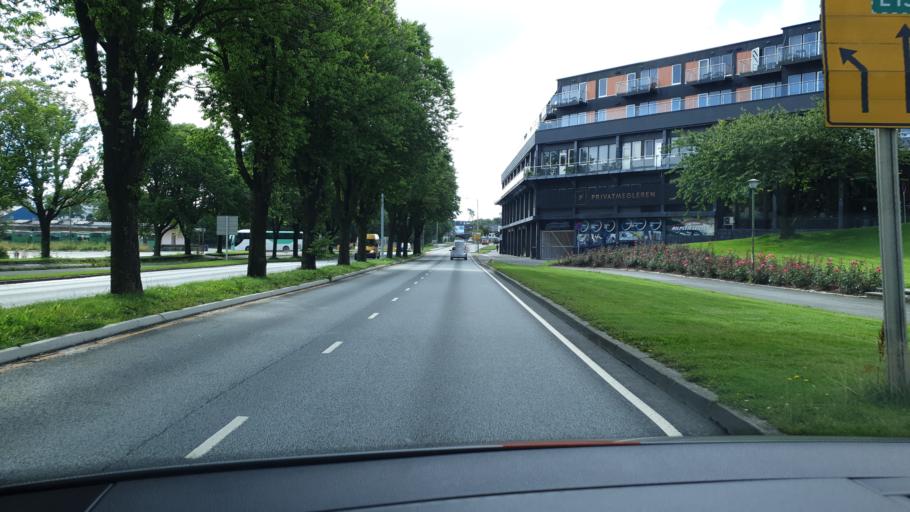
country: NO
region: Rogaland
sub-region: Haugesund
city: Haugesund
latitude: 59.4159
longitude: 5.2735
